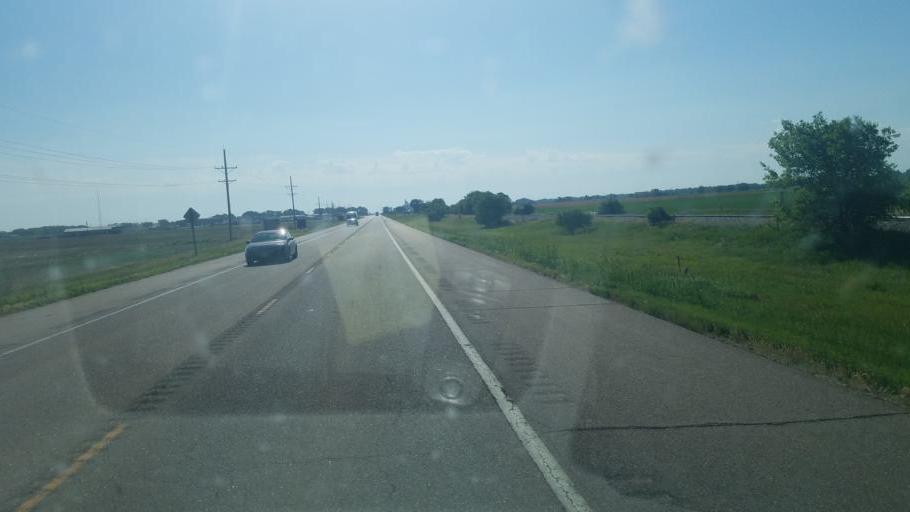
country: US
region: Kansas
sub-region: Barton County
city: Great Bend
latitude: 38.3651
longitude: -98.7063
